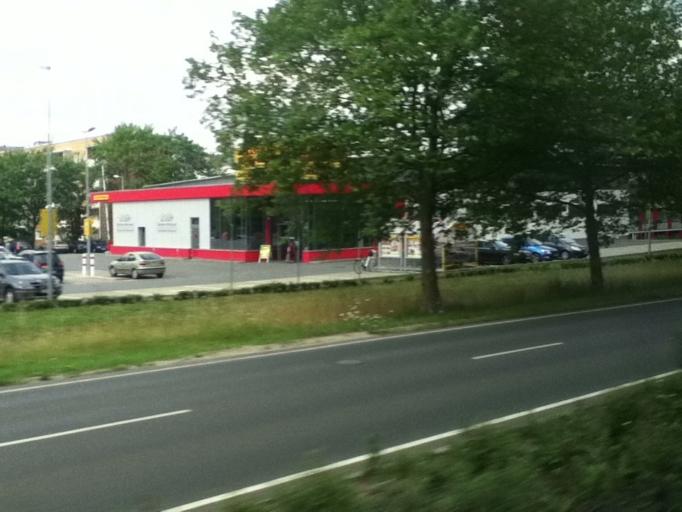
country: DE
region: Thuringia
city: Sulza
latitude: 50.8838
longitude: 11.6149
